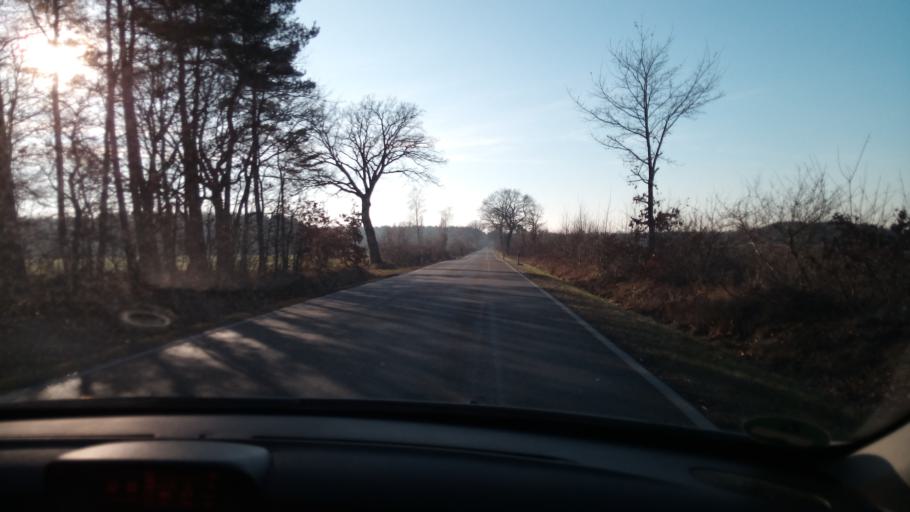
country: DE
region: Schleswig-Holstein
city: Gottin
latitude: 53.5287
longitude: 10.7160
